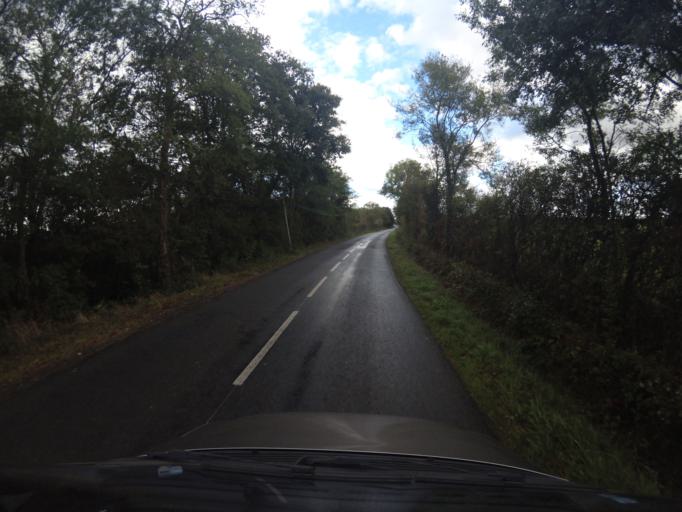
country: FR
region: Pays de la Loire
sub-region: Departement de la Loire-Atlantique
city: Saint-Hilaire-de-Clisson
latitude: 47.0675
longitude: -1.3180
